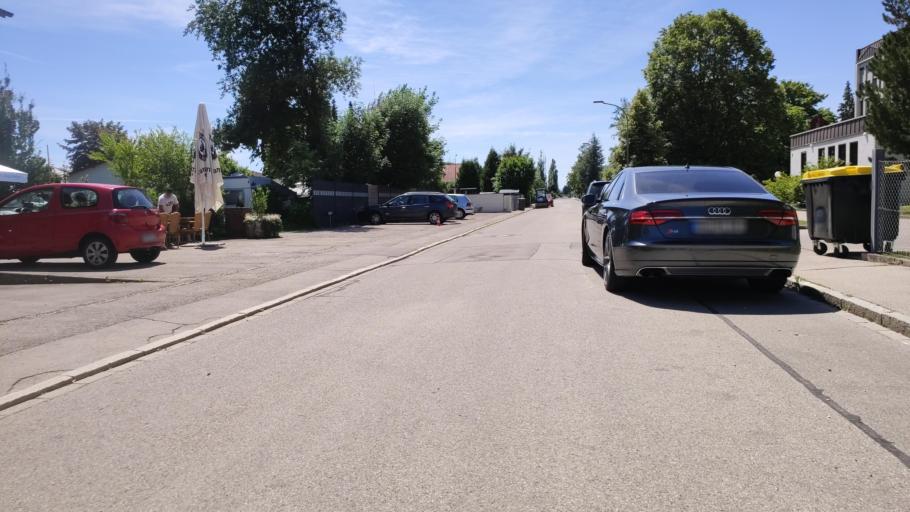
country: DE
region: Bavaria
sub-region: Swabia
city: Bad Worishofen
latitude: 48.0241
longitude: 10.5982
